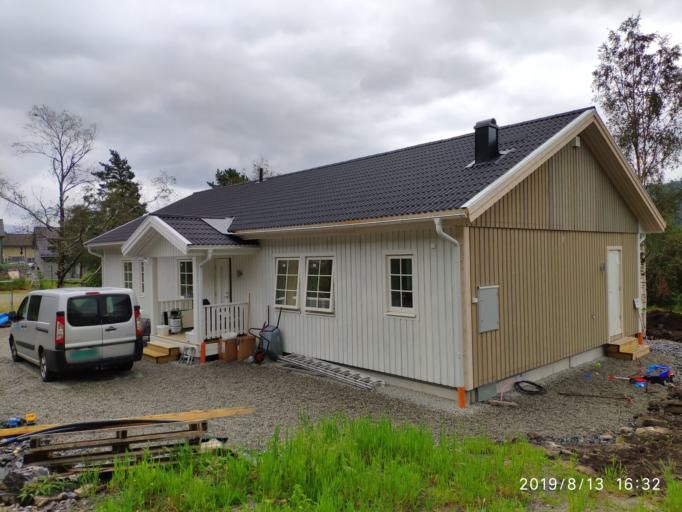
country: NO
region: Hordaland
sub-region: Fusa
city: Eikelandsosen
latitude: 60.2497
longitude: 5.7407
